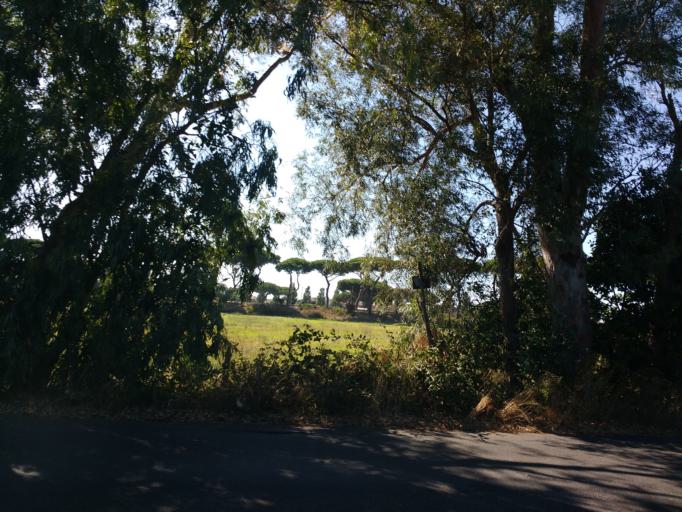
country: IT
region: Latium
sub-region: Citta metropolitana di Roma Capitale
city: Acilia-Castel Fusano-Ostia Antica
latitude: 41.7507
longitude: 12.3300
